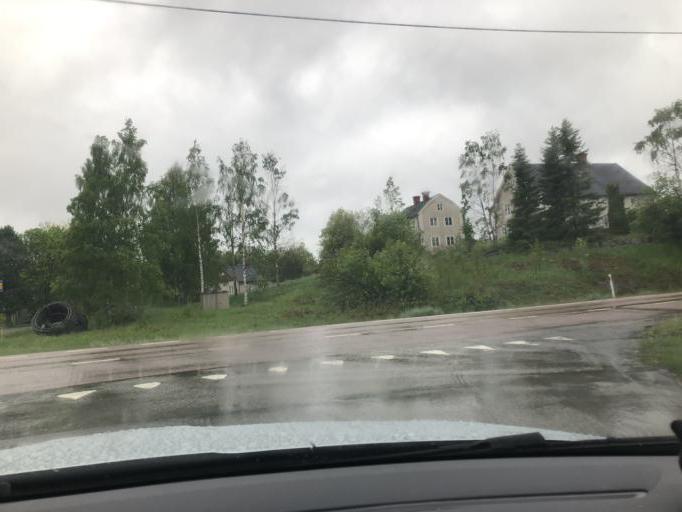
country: SE
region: Vaesternorrland
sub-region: Haernoesands Kommun
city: Haernoesand
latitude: 62.7914
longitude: 17.9135
